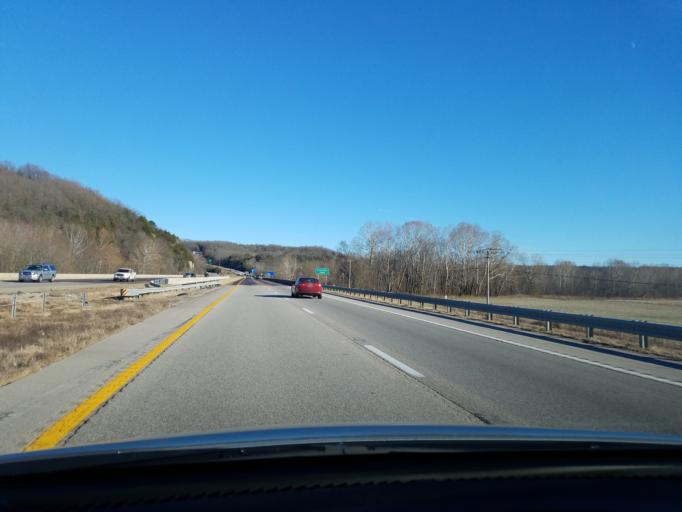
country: US
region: Missouri
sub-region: Pulaski County
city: Waynesville
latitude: 37.8176
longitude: -92.1957
